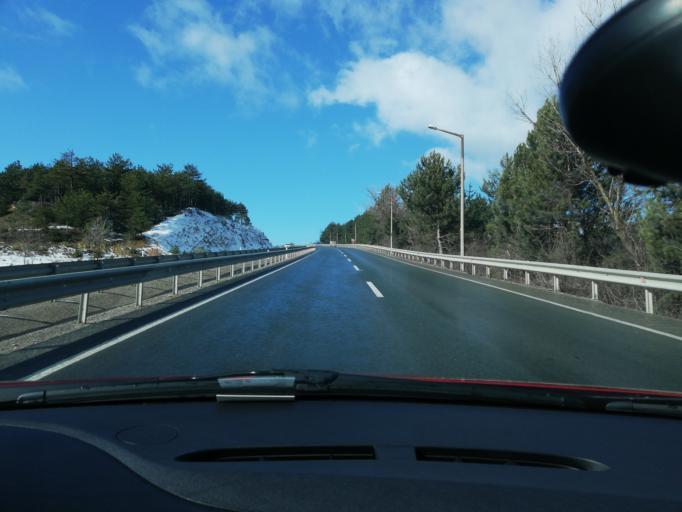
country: TR
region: Kastamonu
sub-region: Cide
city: Kastamonu
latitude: 41.3686
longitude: 33.7526
